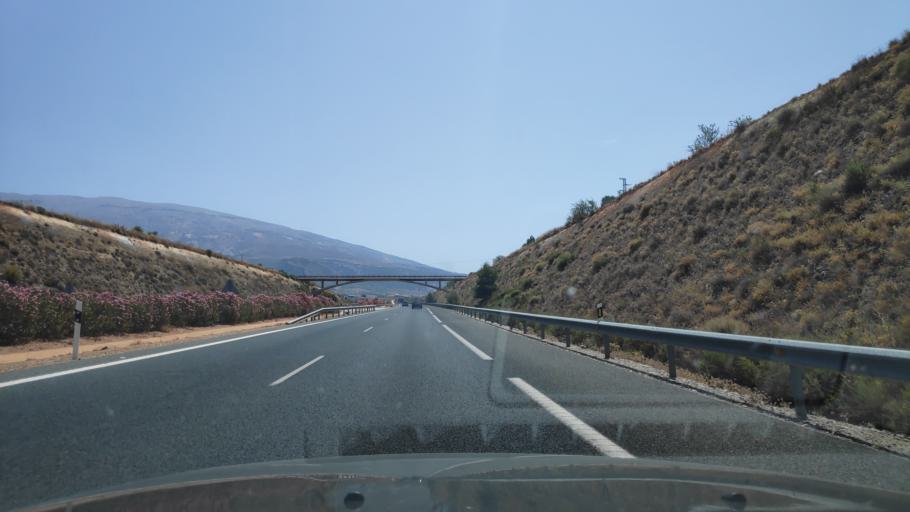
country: ES
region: Andalusia
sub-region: Provincia de Granada
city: Durcal
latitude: 36.9835
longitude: -3.5821
